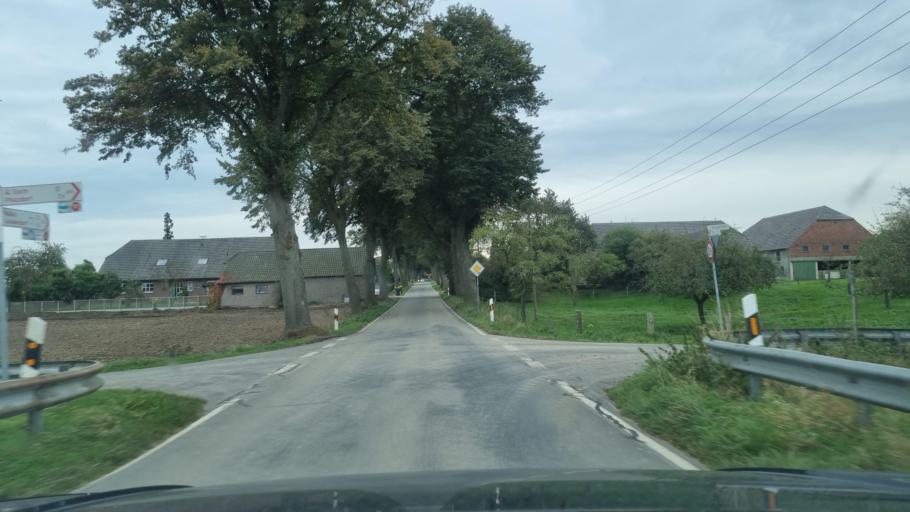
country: DE
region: North Rhine-Westphalia
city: Kalkar
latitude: 51.7322
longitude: 6.2249
